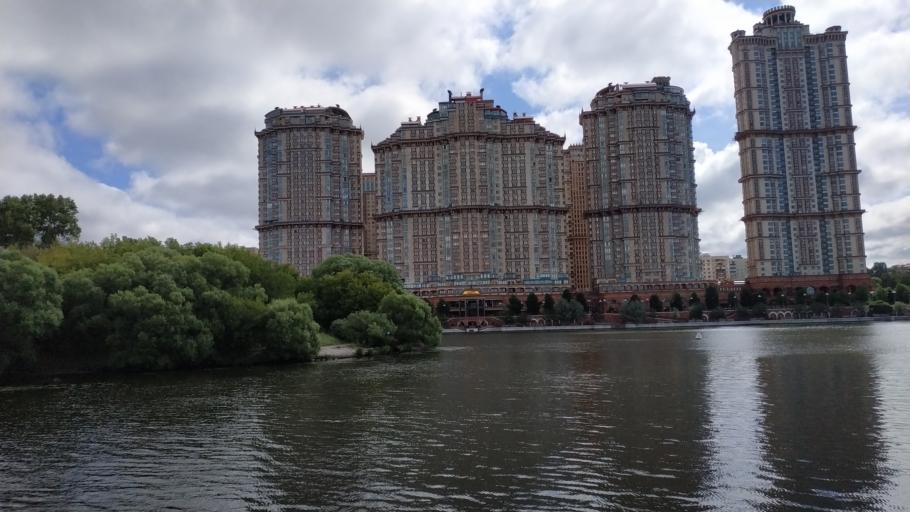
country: RU
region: Moscow
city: Shchukino
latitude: 55.8081
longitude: 37.4432
